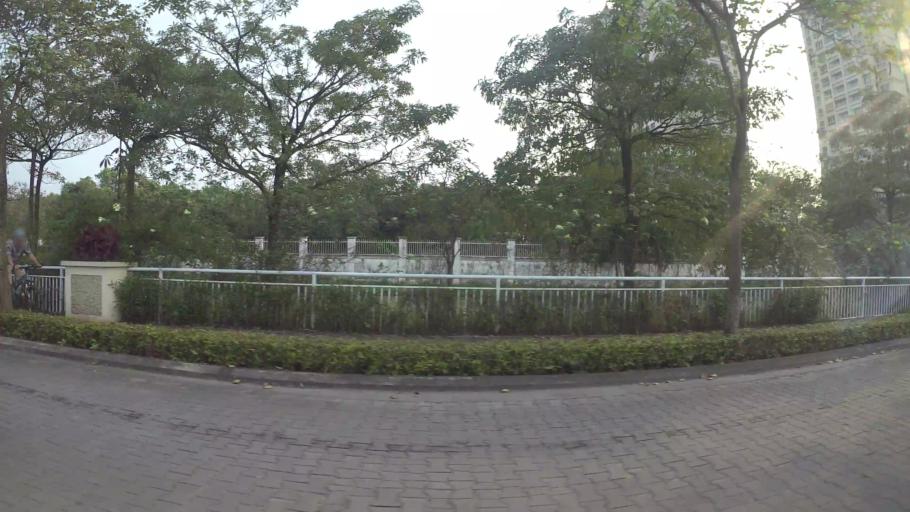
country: VN
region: Ha Noi
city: Tay Ho
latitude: 21.0792
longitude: 105.7941
